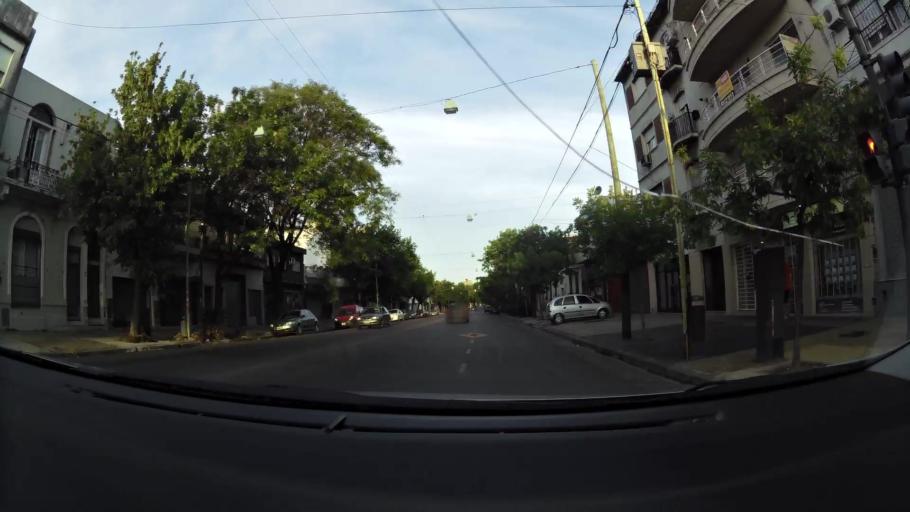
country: AR
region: Buenos Aires F.D.
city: Buenos Aires
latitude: -34.6400
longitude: -58.4222
